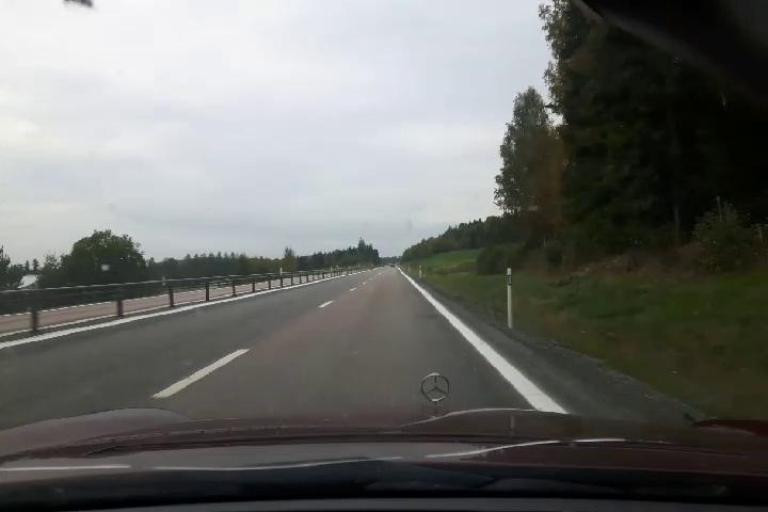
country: SE
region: Vaesternorrland
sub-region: Haernoesands Kommun
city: Haernoesand
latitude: 62.8493
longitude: 18.0035
